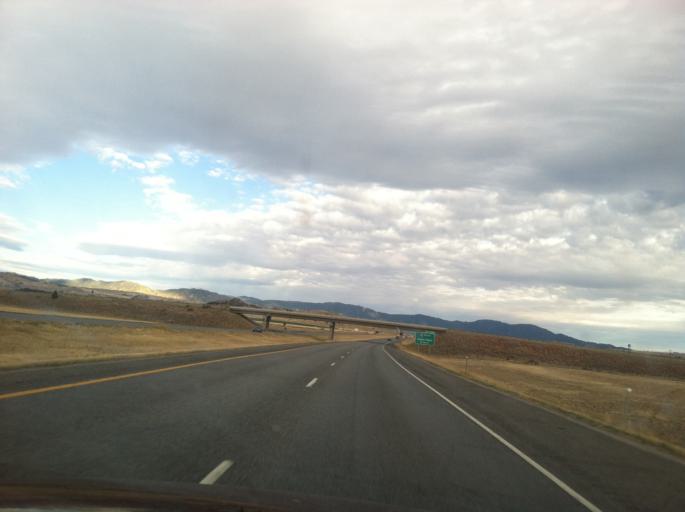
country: US
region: Montana
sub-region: Silver Bow County
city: Butte-Silver Bow (Balance)
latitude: 46.0098
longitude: -112.6868
